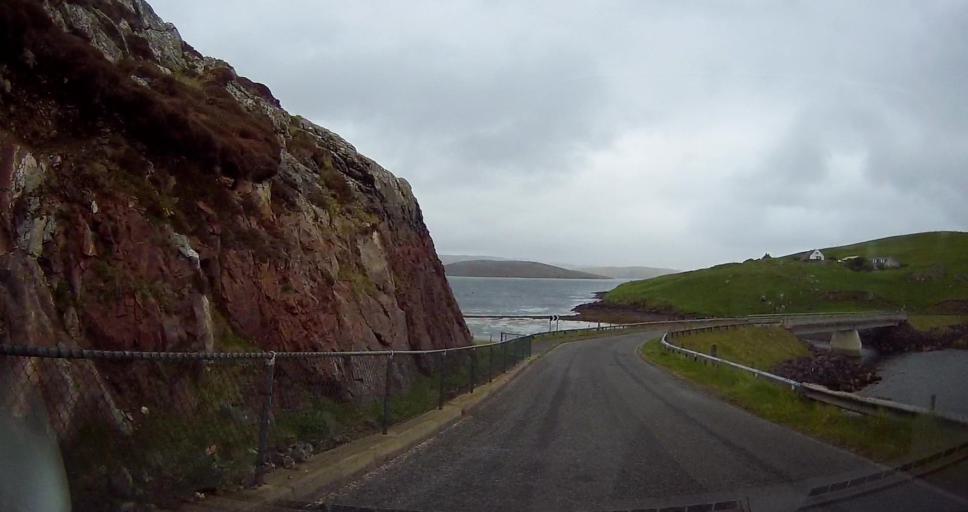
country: GB
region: Scotland
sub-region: Shetland Islands
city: Lerwick
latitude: 60.3779
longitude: -1.3835
